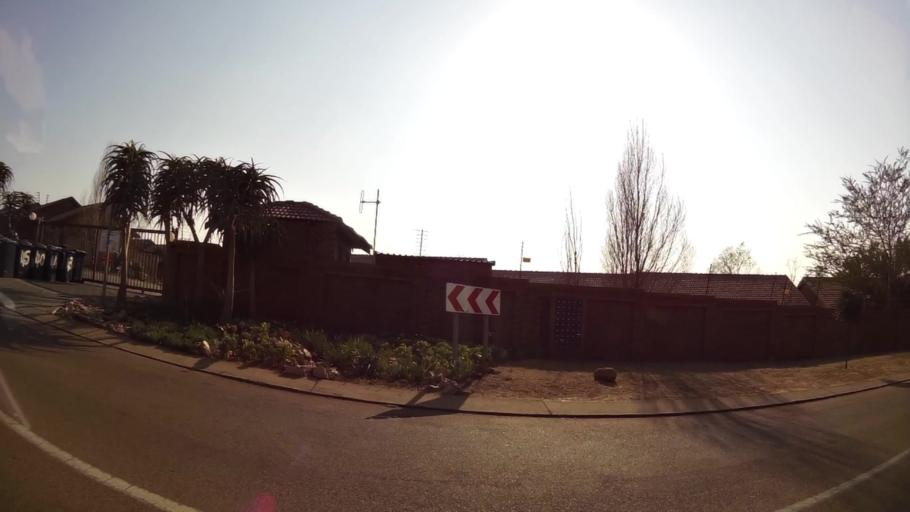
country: ZA
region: Gauteng
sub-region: City of Tshwane Metropolitan Municipality
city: Pretoria
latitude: -25.7588
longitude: 28.3264
